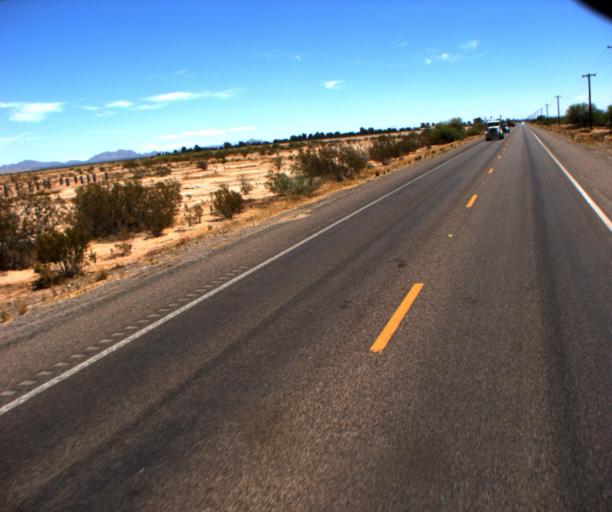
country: US
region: Arizona
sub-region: Pinal County
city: Casa Grande
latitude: 32.8795
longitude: -111.8745
